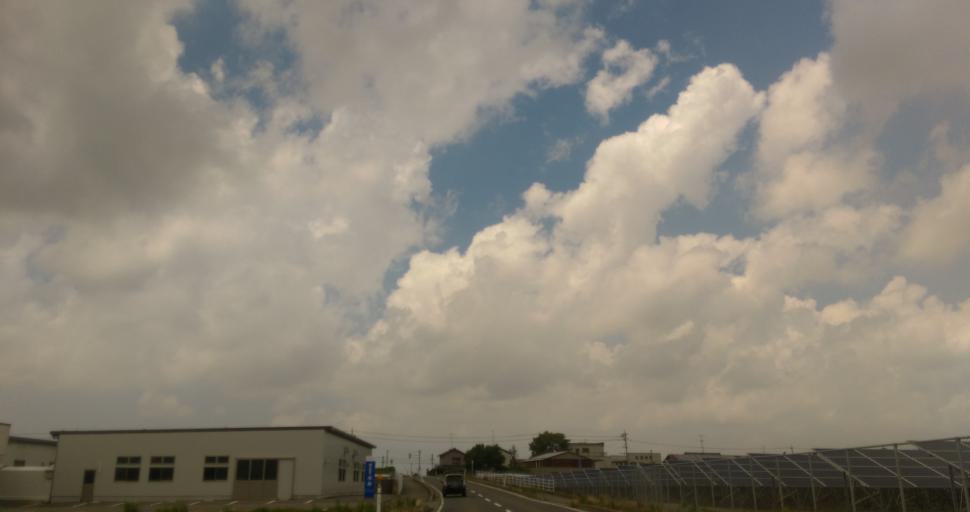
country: JP
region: Fukui
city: Maruoka
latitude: 36.1420
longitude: 136.1881
